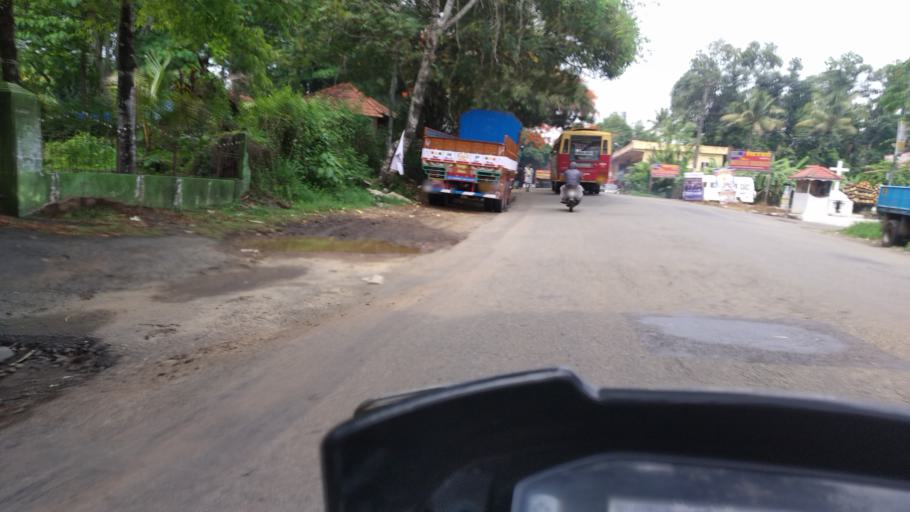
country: IN
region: Kerala
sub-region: Ernakulam
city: Kotamangalam
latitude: 10.0953
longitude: 76.5550
